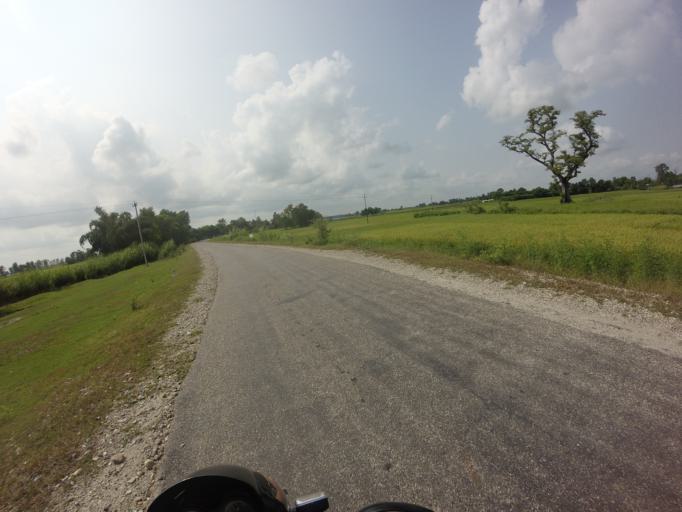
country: NP
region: Far Western
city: Tikapur
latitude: 28.4701
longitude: 81.0737
